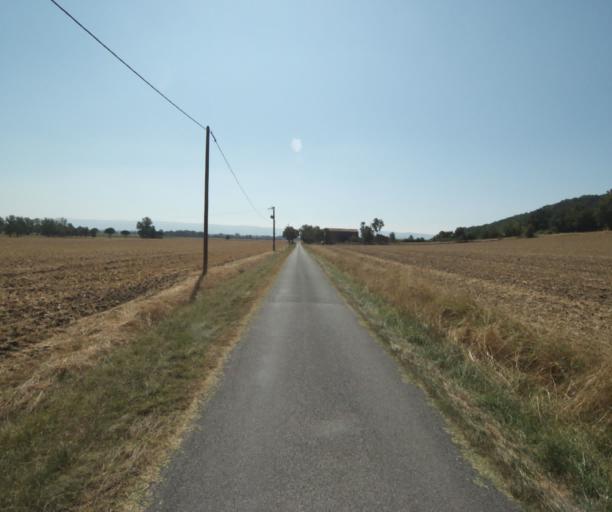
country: FR
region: Midi-Pyrenees
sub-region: Departement de la Haute-Garonne
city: Revel
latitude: 43.5191
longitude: 1.9447
